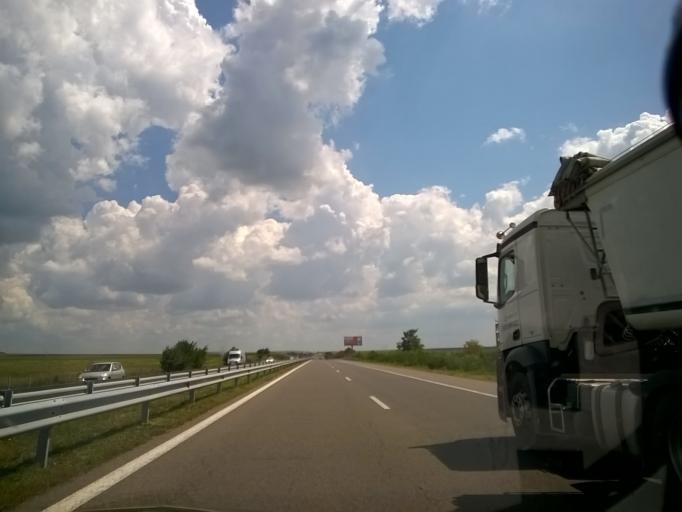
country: BG
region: Burgas
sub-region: Obshtina Karnobat
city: Karnobat
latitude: 42.5893
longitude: 27.0291
